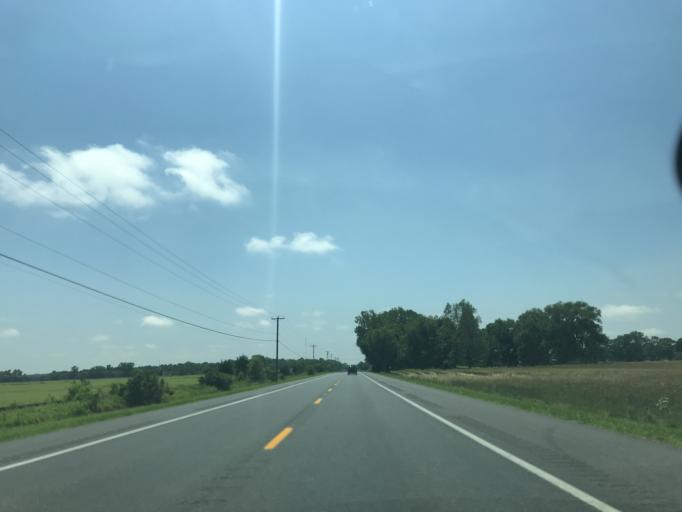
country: US
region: Maryland
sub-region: Dorchester County
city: Hurlock
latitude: 38.6033
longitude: -75.9080
